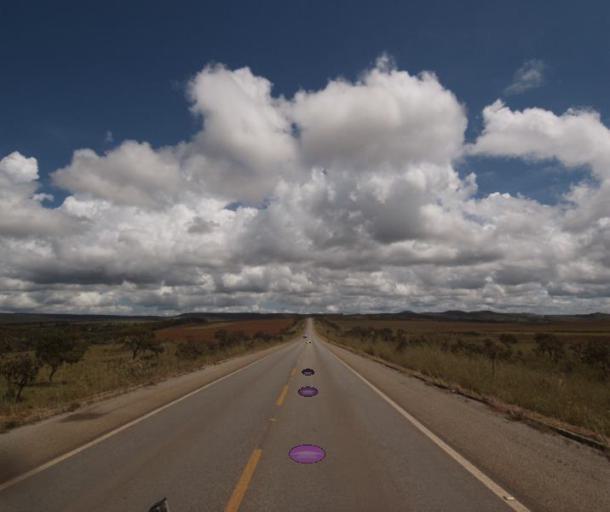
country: BR
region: Goias
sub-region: Pirenopolis
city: Pirenopolis
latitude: -15.7572
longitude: -48.6864
